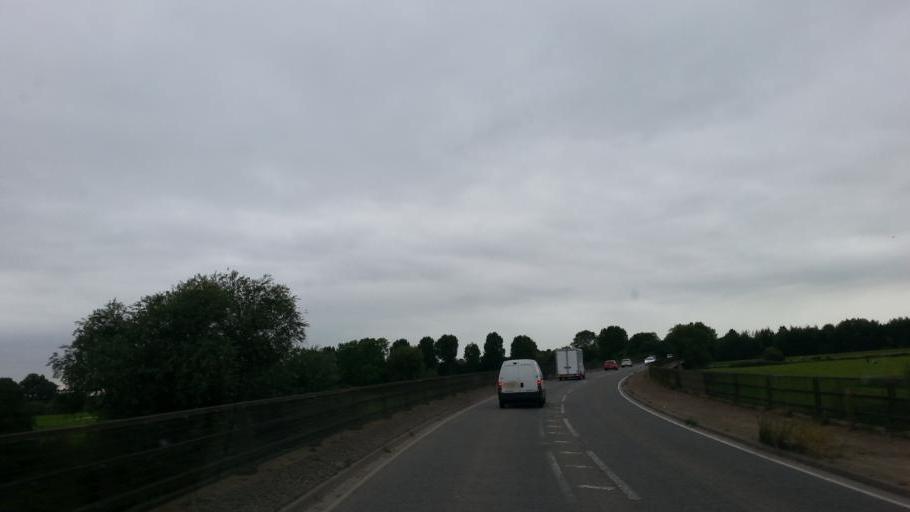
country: GB
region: England
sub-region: Cambridgeshire
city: Hemingford Grey
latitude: 52.3194
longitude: -0.0699
